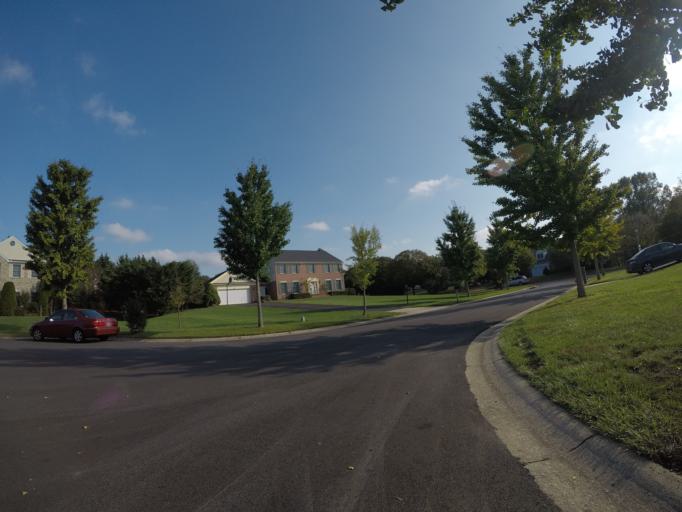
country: US
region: Maryland
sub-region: Howard County
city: Columbia
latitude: 39.2644
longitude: -76.8460
